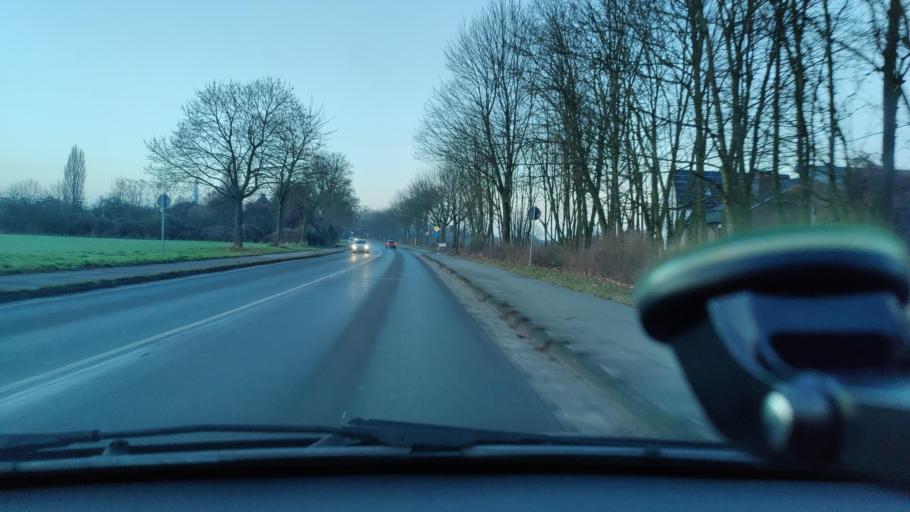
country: DE
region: North Rhine-Westphalia
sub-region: Regierungsbezirk Dusseldorf
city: Dinslaken
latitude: 51.5572
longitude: 6.7105
